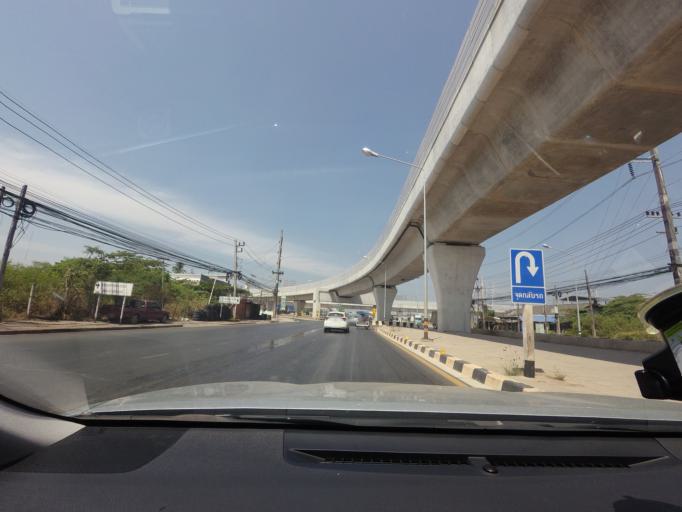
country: TH
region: Surat Thani
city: Surat Thani
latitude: 9.1511
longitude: 99.3703
